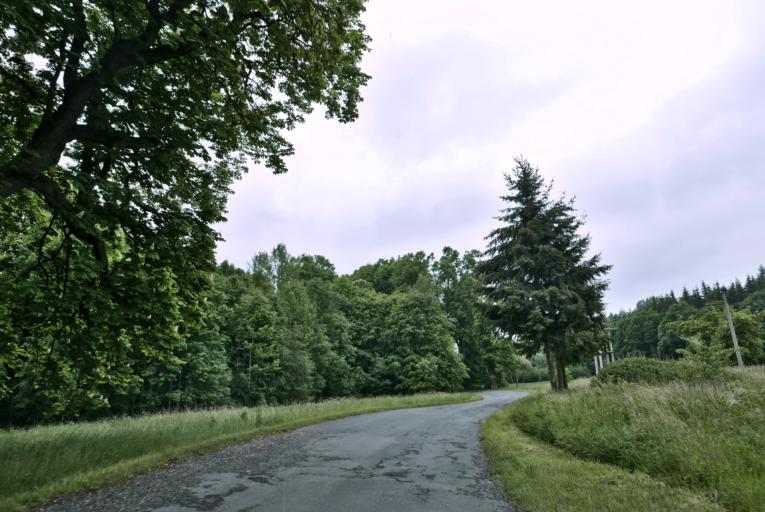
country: CZ
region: Plzensky
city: Kralovice
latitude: 49.9849
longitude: 13.4268
